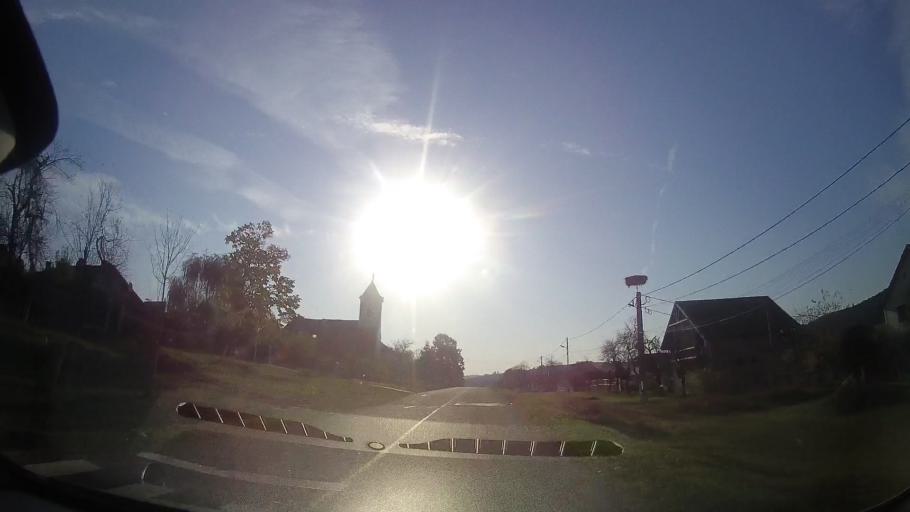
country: RO
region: Timis
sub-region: Comuna Bogda
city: Bogda
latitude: 45.9797
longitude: 21.5746
